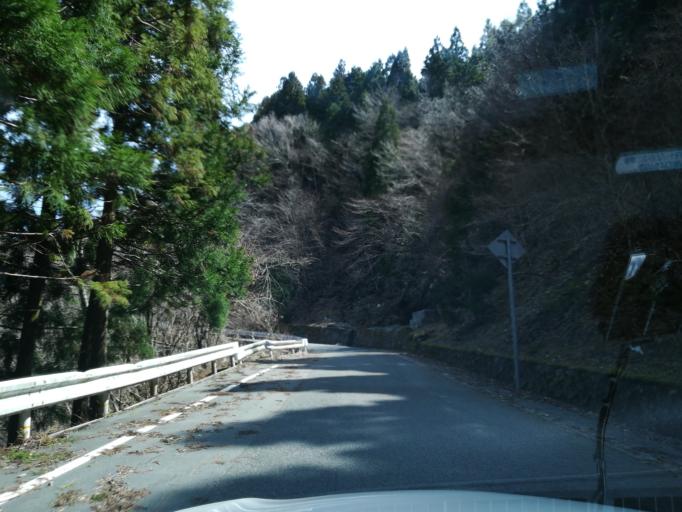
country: JP
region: Tokushima
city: Wakimachi
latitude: 33.8848
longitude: 134.0472
